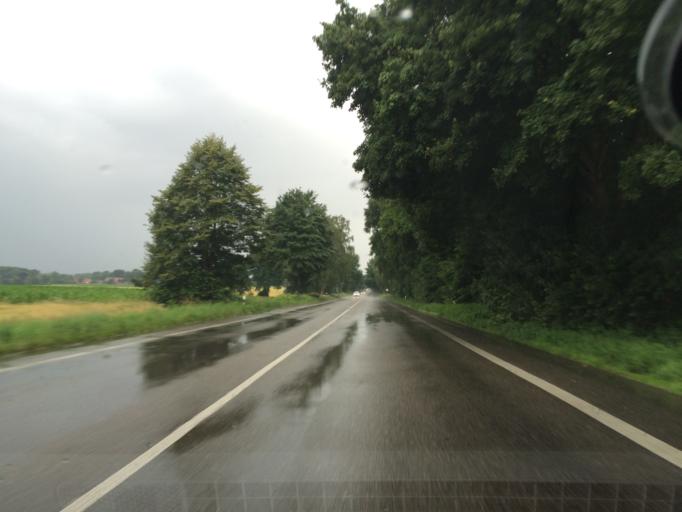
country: DE
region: North Rhine-Westphalia
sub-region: Regierungsbezirk Munster
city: Haltern
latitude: 51.7771
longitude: 7.2058
